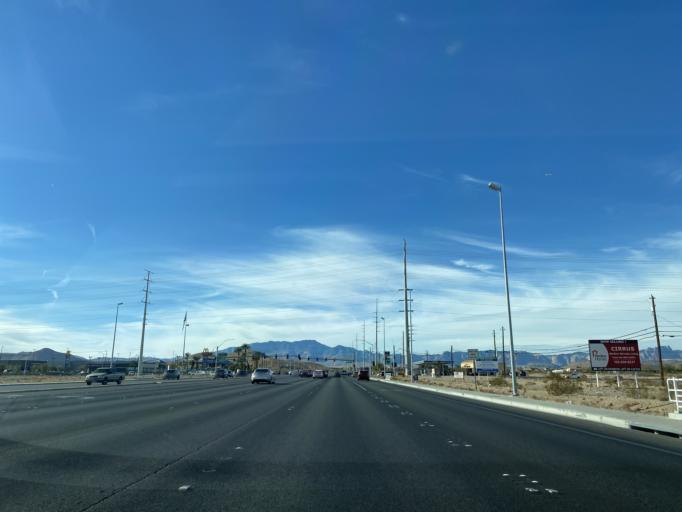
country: US
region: Nevada
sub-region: Clark County
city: Enterprise
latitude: 36.0230
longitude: -115.2412
